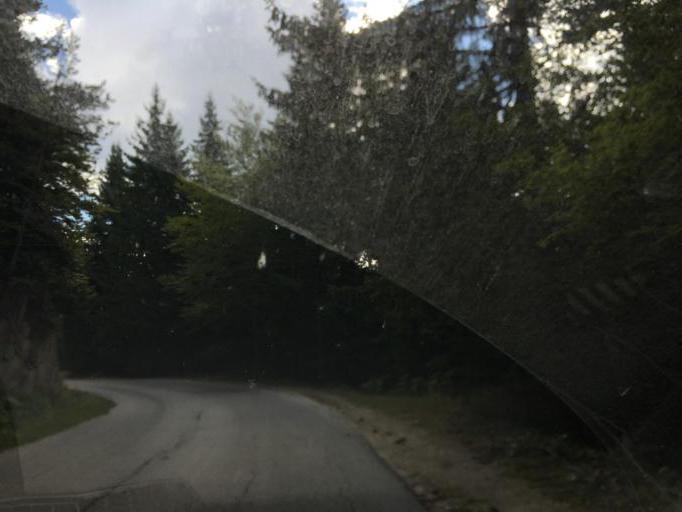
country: BG
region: Pazardzhik
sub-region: Obshtina Batak
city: Batak
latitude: 41.9132
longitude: 24.2850
